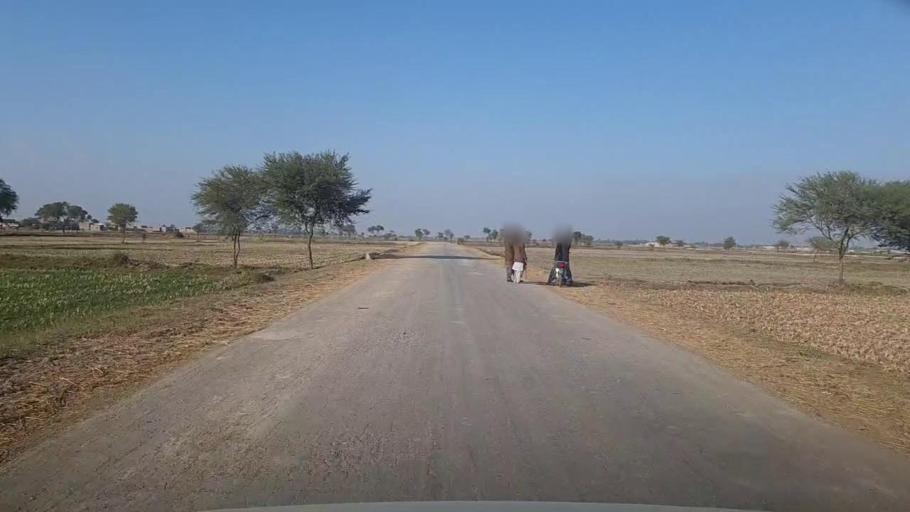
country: PK
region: Sindh
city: Phulji
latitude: 26.8641
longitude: 67.7947
